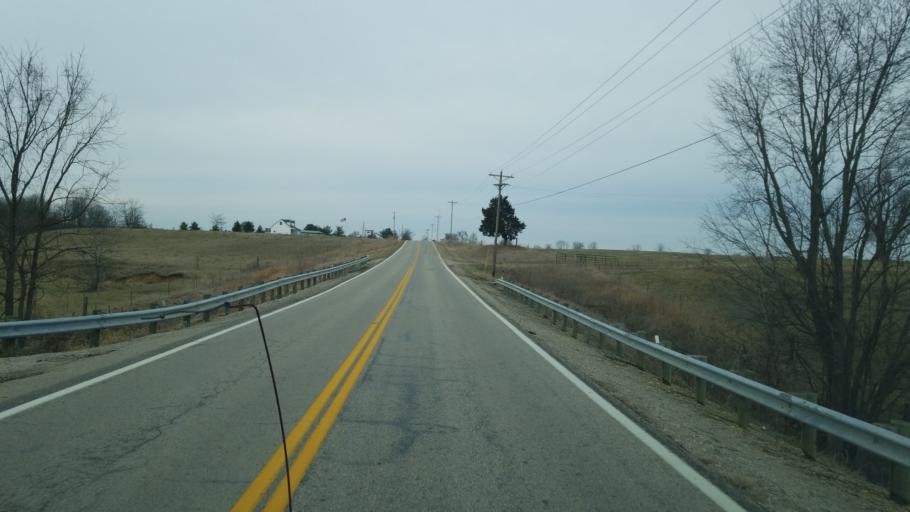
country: US
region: Ohio
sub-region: Pickaway County
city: Williamsport
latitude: 39.5396
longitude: -83.1229
